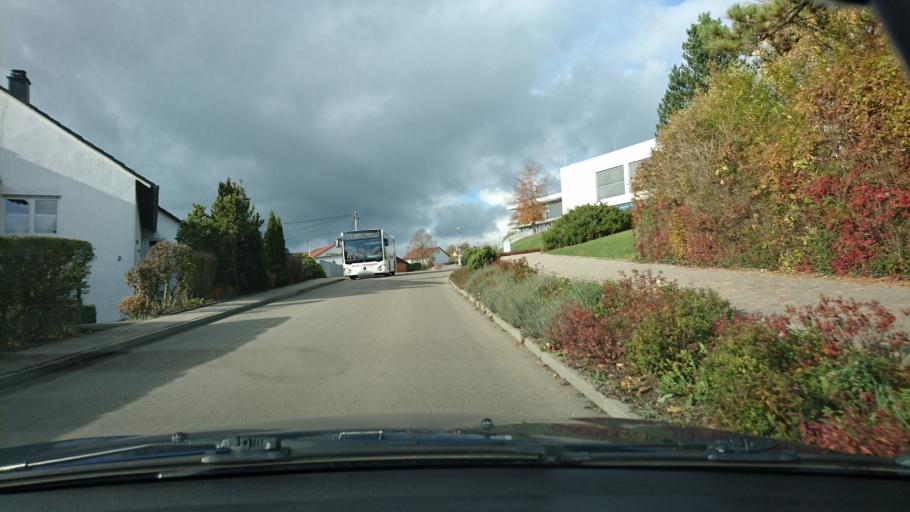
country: DE
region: Baden-Wuerttemberg
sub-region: Regierungsbezirk Stuttgart
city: Neresheim
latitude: 48.7564
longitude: 10.3273
